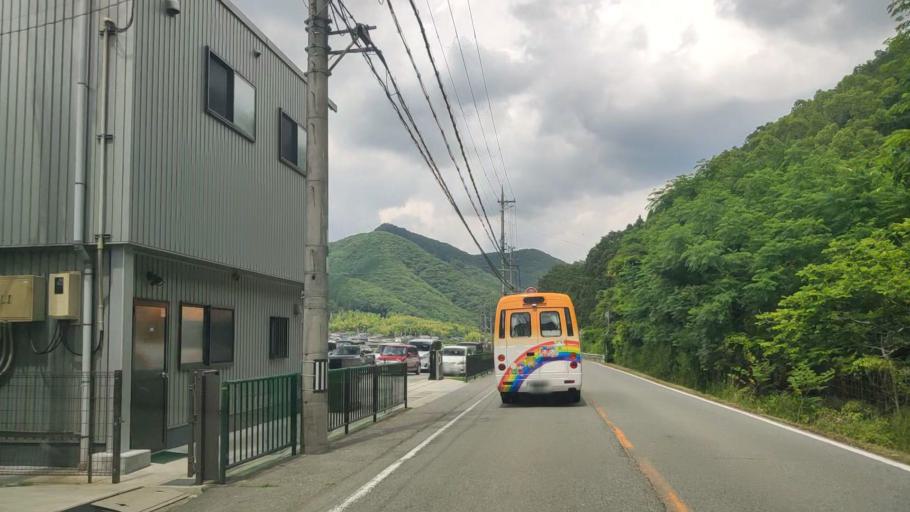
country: JP
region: Hyogo
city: Yamazakicho-nakabirose
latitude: 34.9386
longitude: 134.4846
